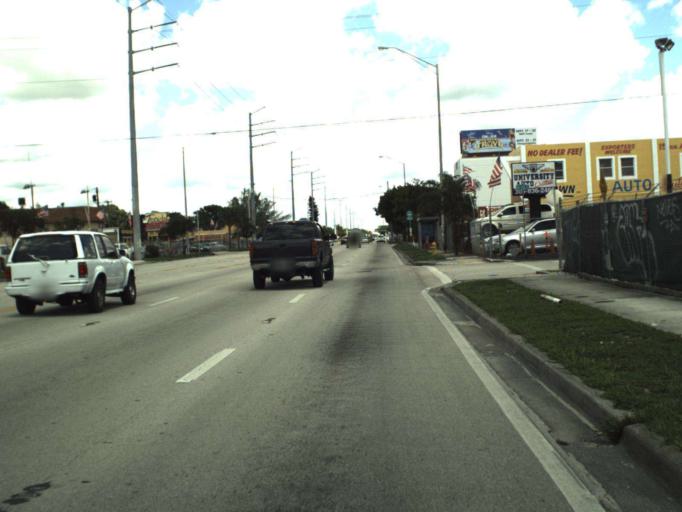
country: US
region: Florida
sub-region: Miami-Dade County
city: Pinewood
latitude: 25.8780
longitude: -80.2102
